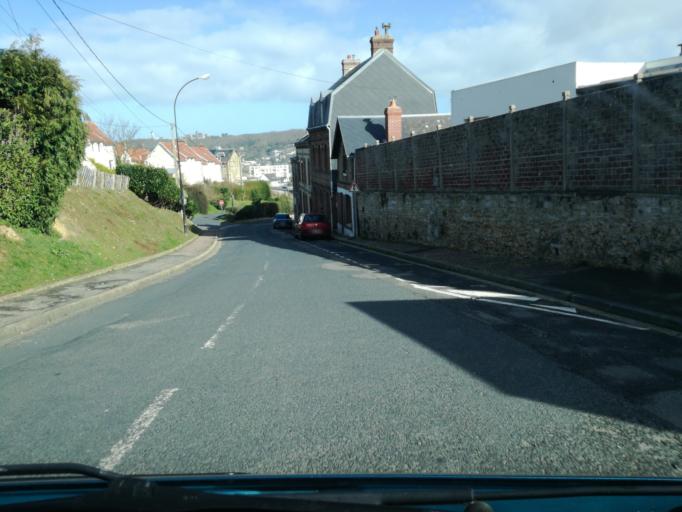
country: FR
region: Haute-Normandie
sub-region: Departement de la Seine-Maritime
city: Fecamp
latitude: 49.7512
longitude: 0.3702
